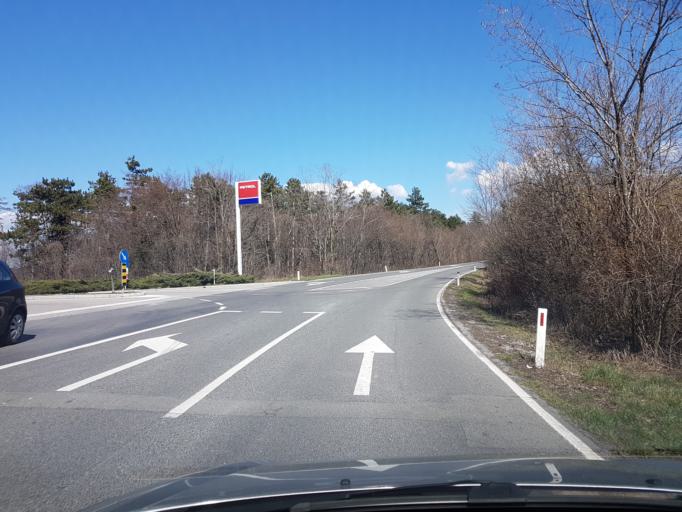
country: SI
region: Sezana
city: Sezana
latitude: 45.6552
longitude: 13.8817
